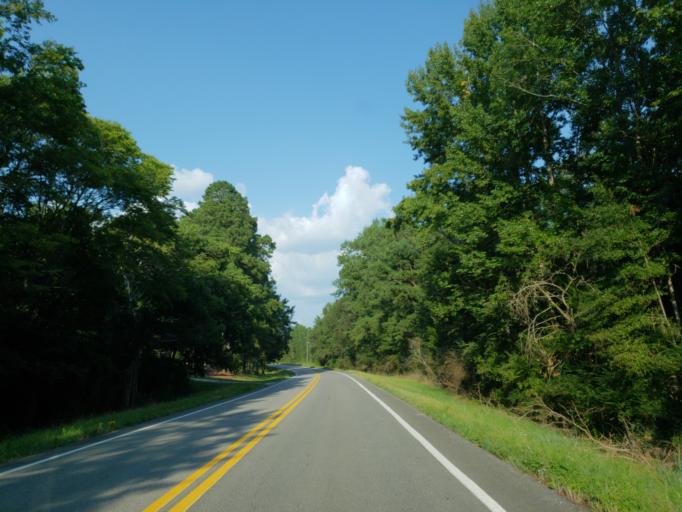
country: US
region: Alabama
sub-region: Greene County
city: Eutaw
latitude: 32.7585
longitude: -88.0146
